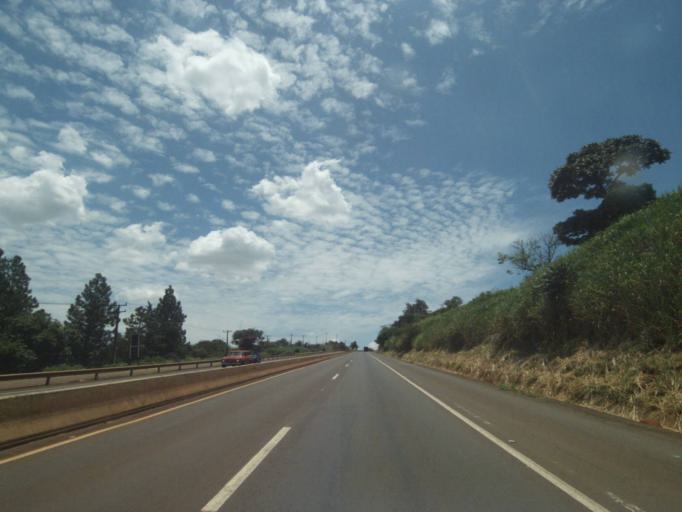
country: BR
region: Parana
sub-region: Londrina
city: Londrina
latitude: -23.3776
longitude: -51.1373
